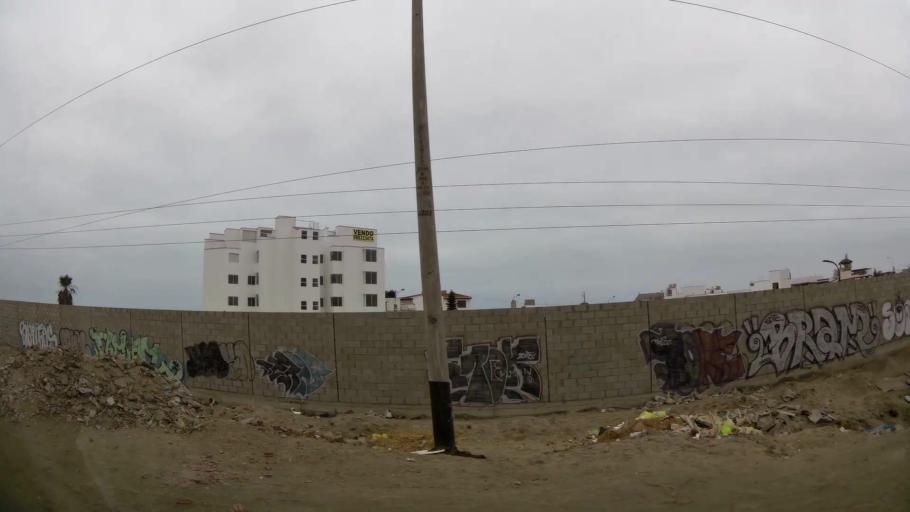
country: PE
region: Lima
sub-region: Lima
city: Punta Hermosa
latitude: -12.3378
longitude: -76.8179
